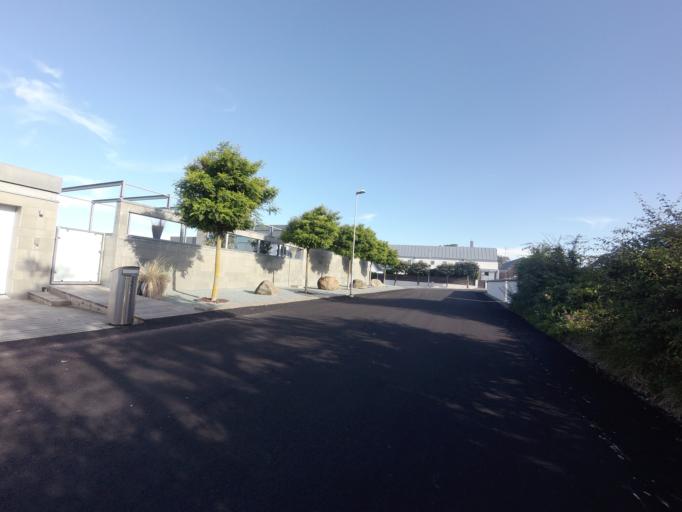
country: SE
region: Skane
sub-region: Hoganas Kommun
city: Hoganas
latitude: 56.1717
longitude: 12.5619
